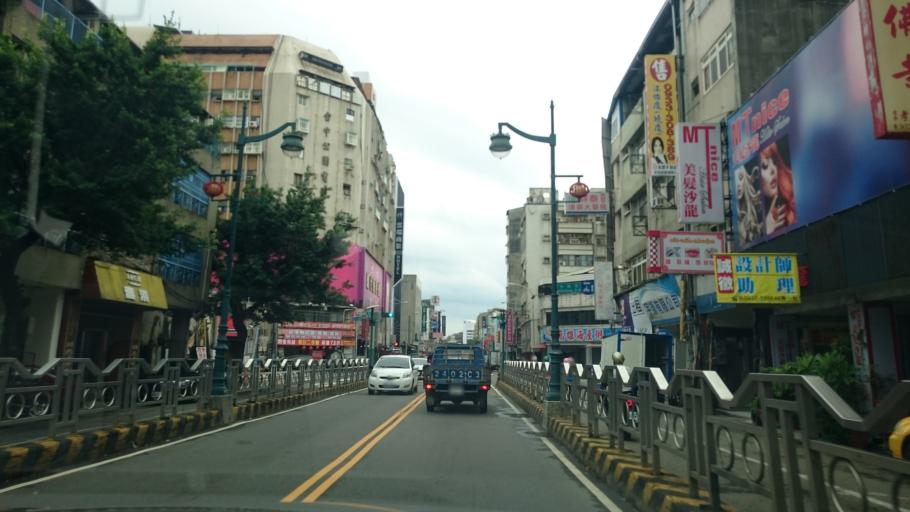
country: TW
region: Taiwan
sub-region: Taichung City
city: Taichung
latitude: 24.1466
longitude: 120.6794
